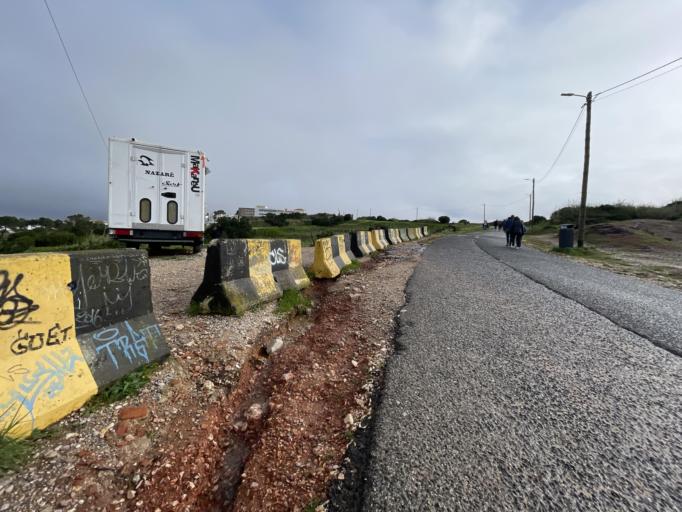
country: PT
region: Leiria
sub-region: Nazare
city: Nazare
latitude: 39.6052
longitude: -9.0816
